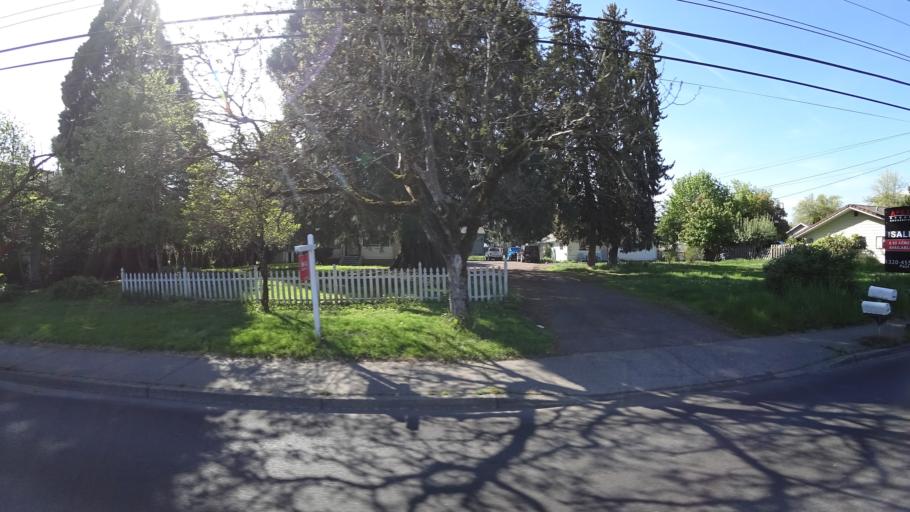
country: US
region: Oregon
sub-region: Washington County
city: Hillsboro
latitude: 45.5269
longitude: -122.9695
